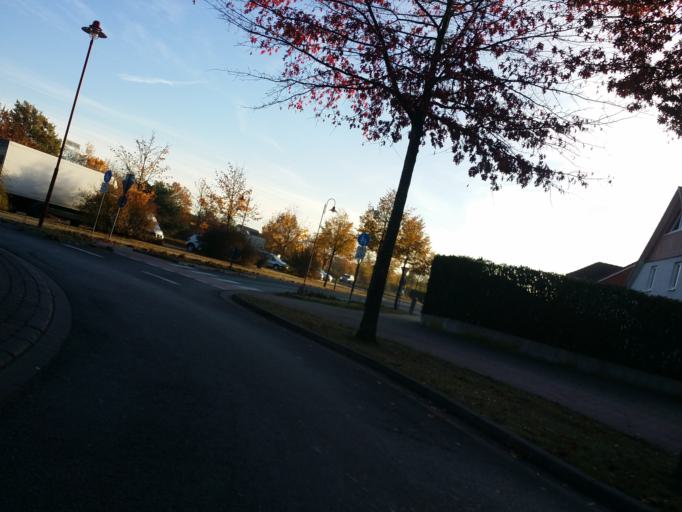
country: DE
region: Lower Saxony
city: Stuhr
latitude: 53.0019
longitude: 8.7764
